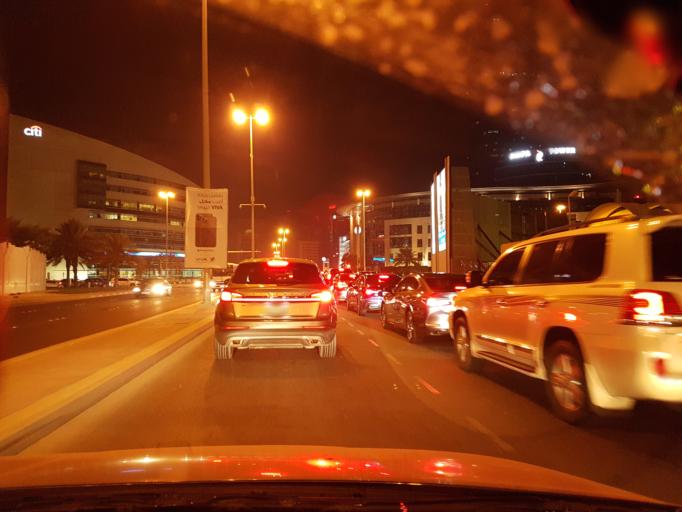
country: BH
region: Manama
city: Jidd Hafs
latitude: 26.2346
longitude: 50.5450
